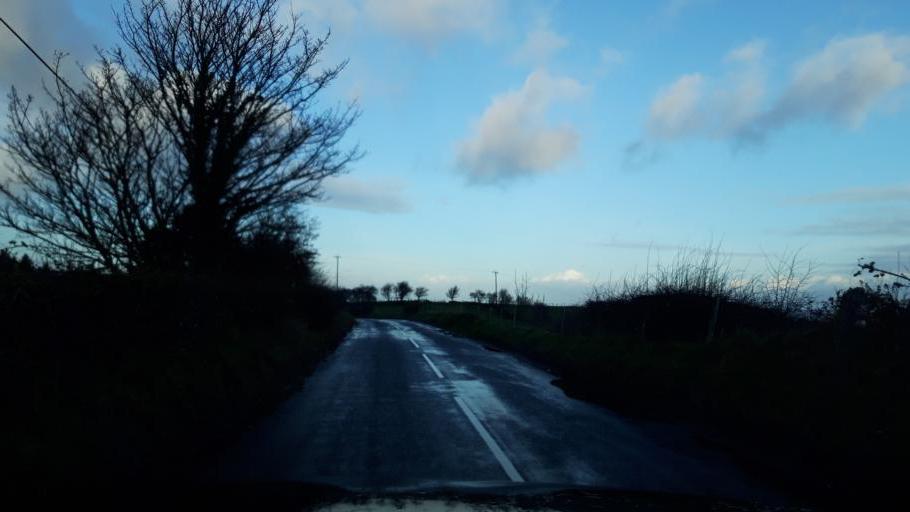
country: GB
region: Northern Ireland
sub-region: Moyle District
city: Ballycastle
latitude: 55.1967
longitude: -6.2271
